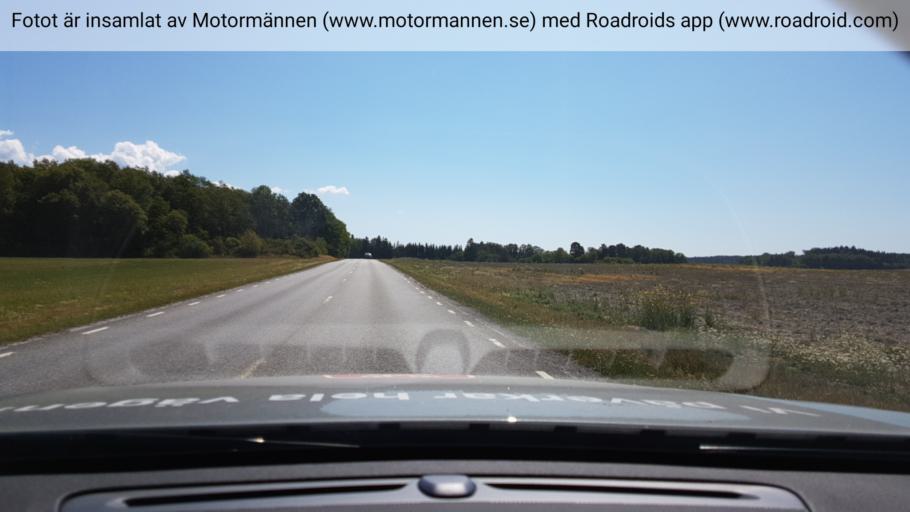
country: SE
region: Stockholm
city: Stenhamra
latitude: 59.3439
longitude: 17.7239
